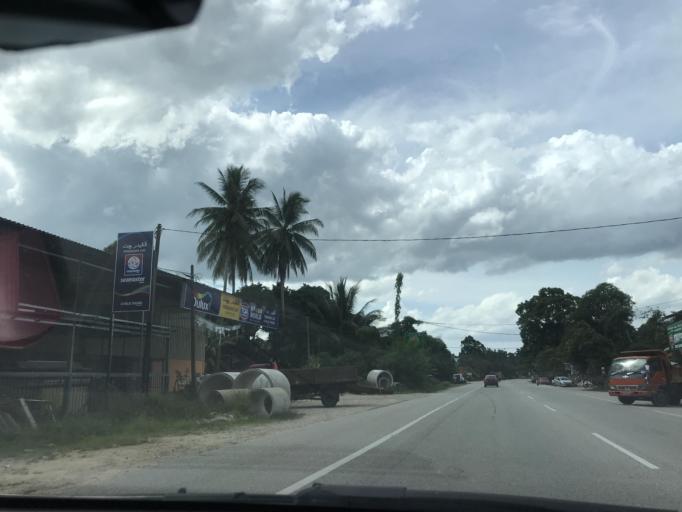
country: MY
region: Kelantan
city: Kampong Pangkal Kalong
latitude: 5.9150
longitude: 102.1880
